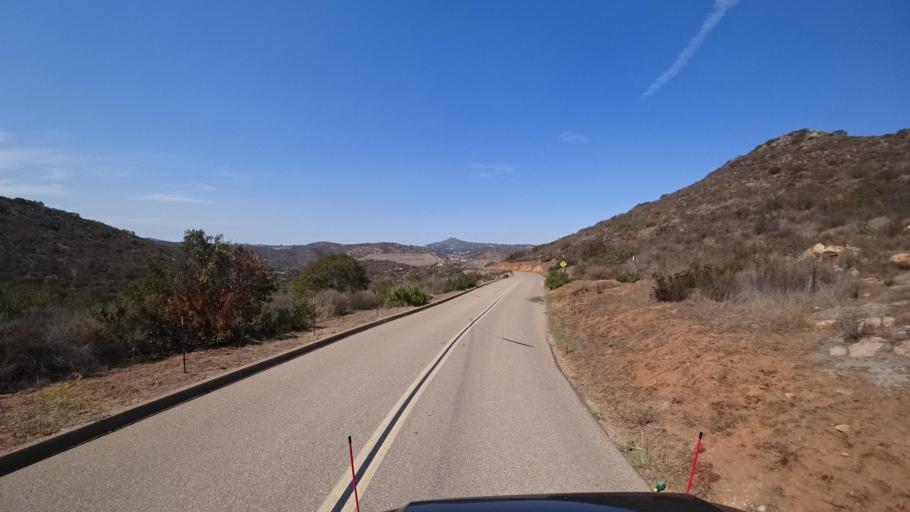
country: US
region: California
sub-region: San Diego County
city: Rancho San Diego
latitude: 32.7245
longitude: -116.9332
